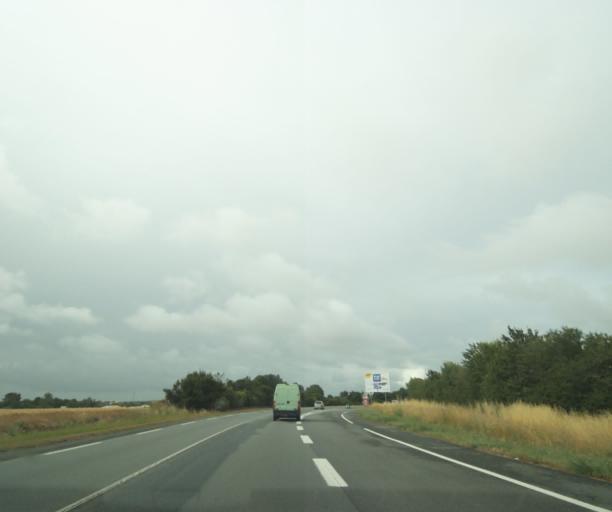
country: FR
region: Poitou-Charentes
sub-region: Departement de la Charente-Maritime
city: Lagord
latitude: 46.1935
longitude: -1.1413
